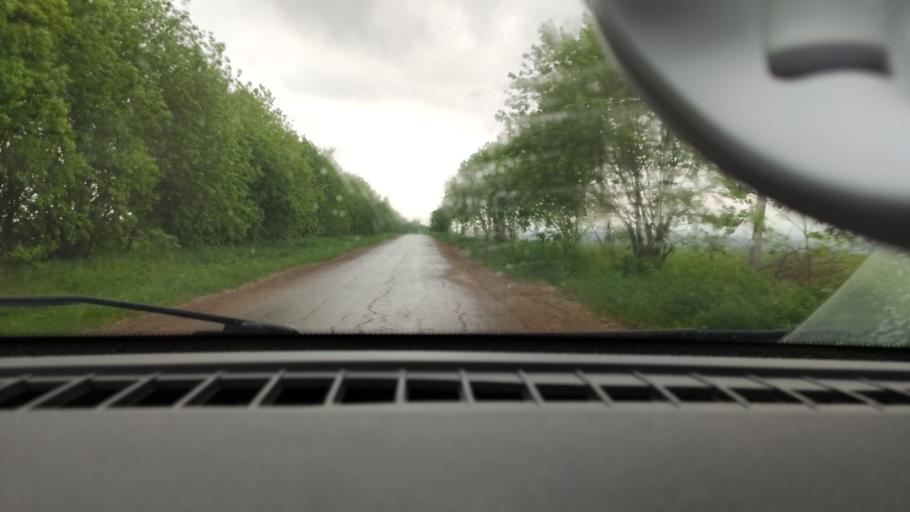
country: RU
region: Perm
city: Gamovo
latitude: 57.8525
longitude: 56.0793
